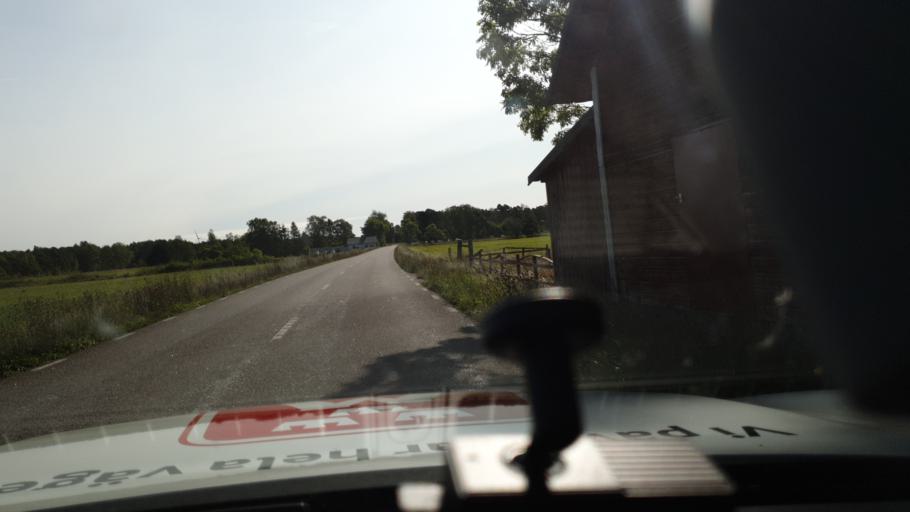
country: SE
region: Gotland
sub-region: Gotland
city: Hemse
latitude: 57.1126
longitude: 18.2845
